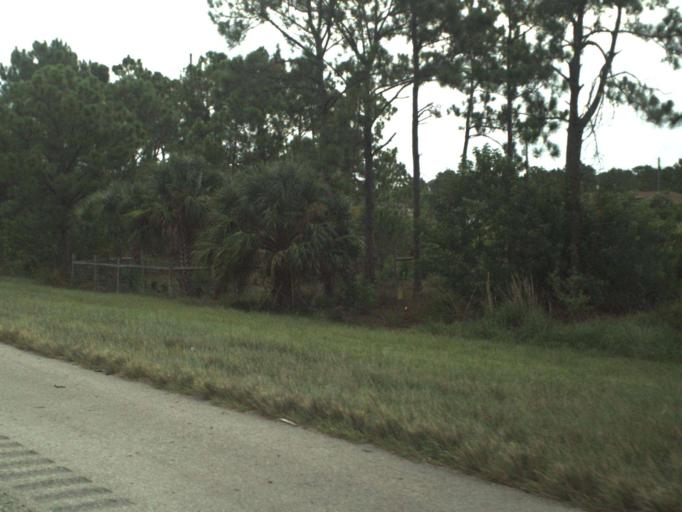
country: US
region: Florida
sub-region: Saint Lucie County
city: Port Saint Lucie
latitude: 27.2829
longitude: -80.4247
